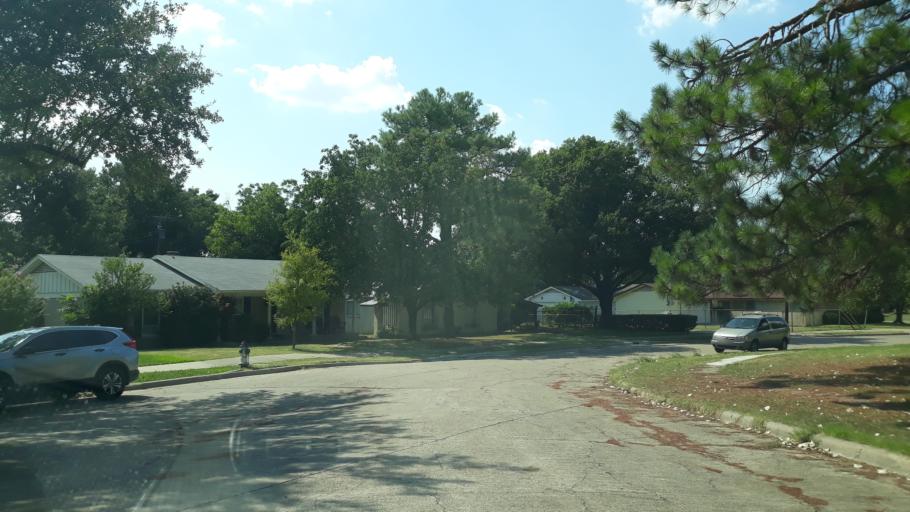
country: US
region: Texas
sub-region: Dallas County
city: Irving
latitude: 32.8496
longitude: -96.9962
